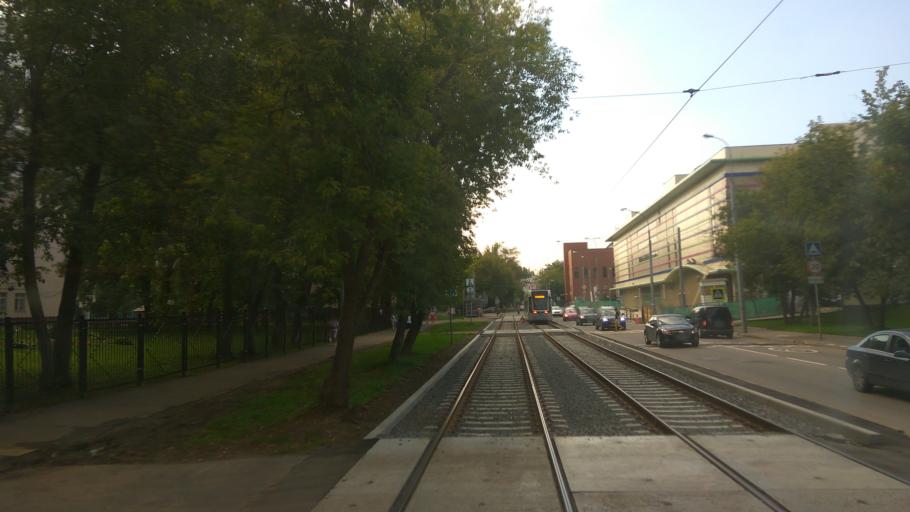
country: RU
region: Moskovskaya
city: Koptevo
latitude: 55.8246
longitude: 37.5167
